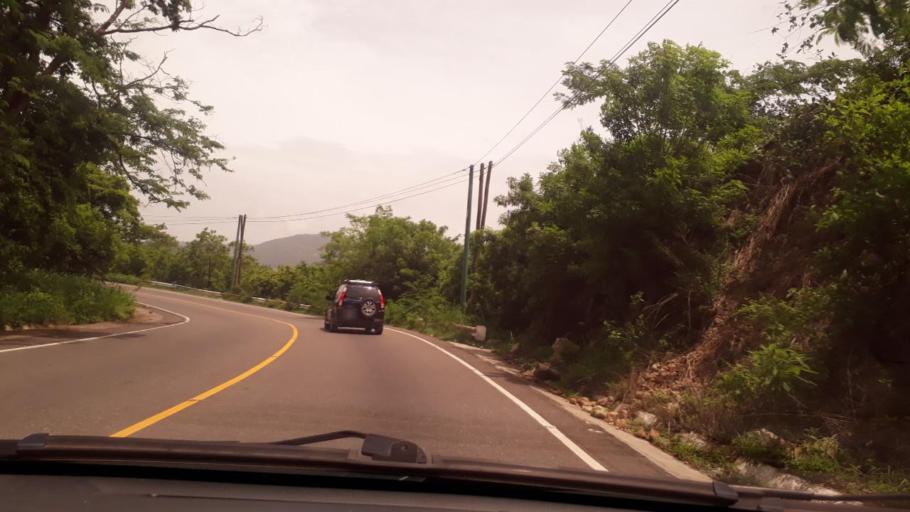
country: GT
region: Chiquimula
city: San Jacinto
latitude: 14.6569
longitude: -89.4899
